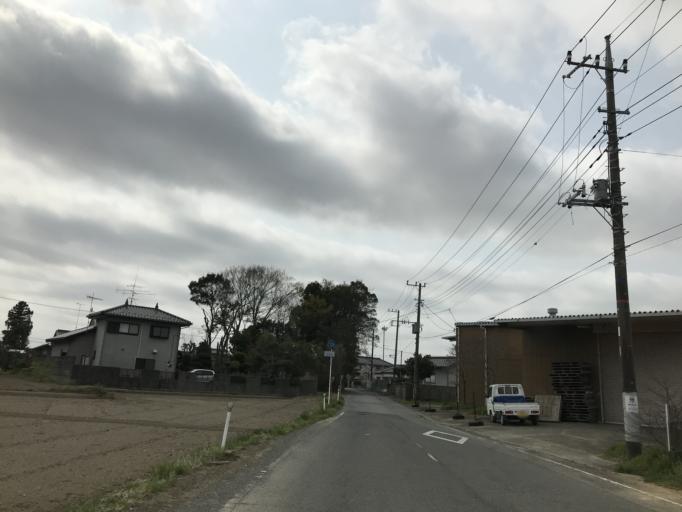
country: JP
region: Ibaraki
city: Mitsukaido
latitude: 36.0266
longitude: 140.0071
